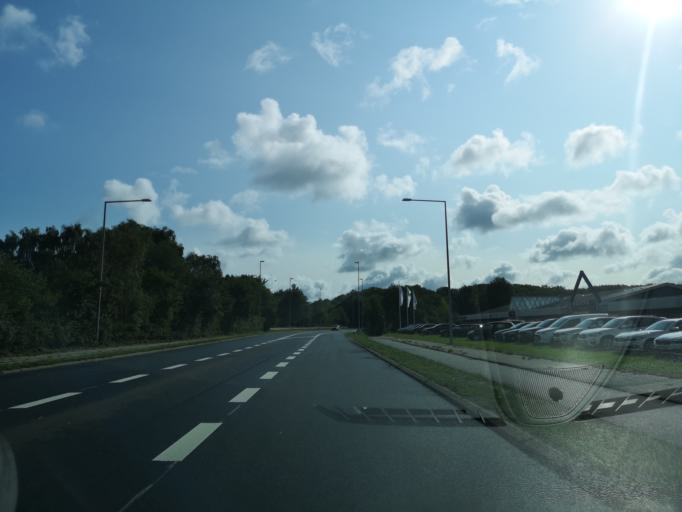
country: DK
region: Central Jutland
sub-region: Herning Kommune
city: Snejbjerg
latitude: 56.1351
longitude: 8.9355
